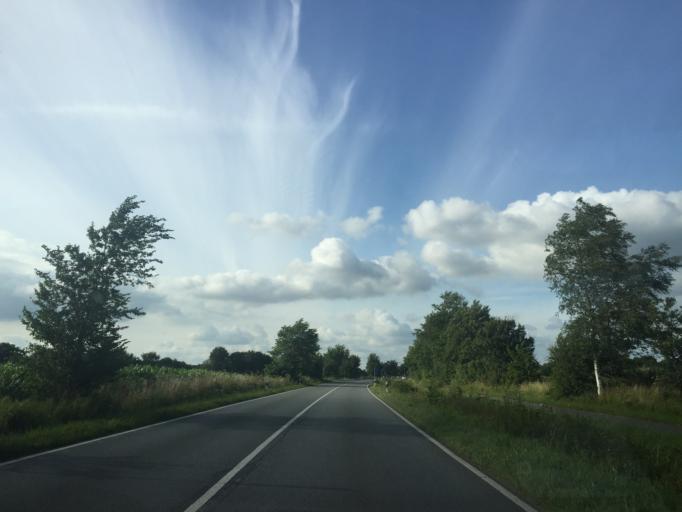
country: DE
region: Schleswig-Holstein
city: Harrislee
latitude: 54.7865
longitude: 9.3717
